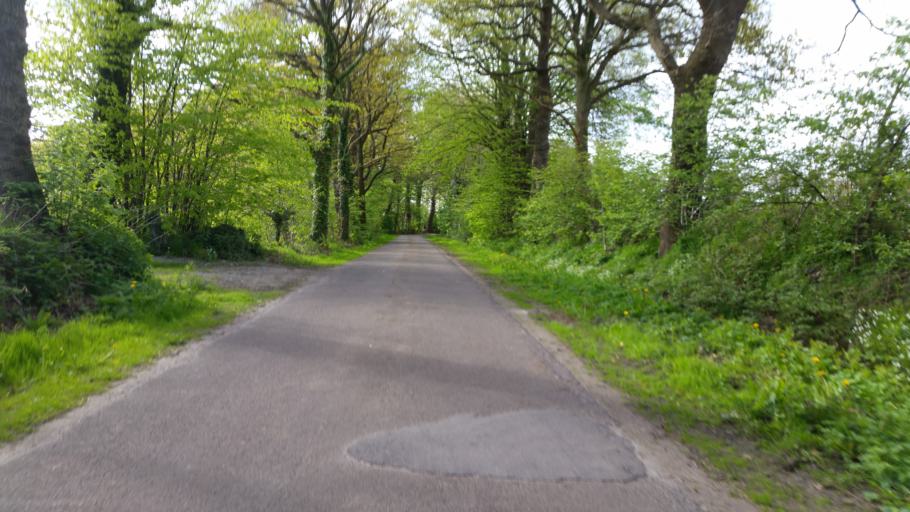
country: DE
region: Lower Saxony
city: Aurich
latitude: 53.4528
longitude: 7.4897
